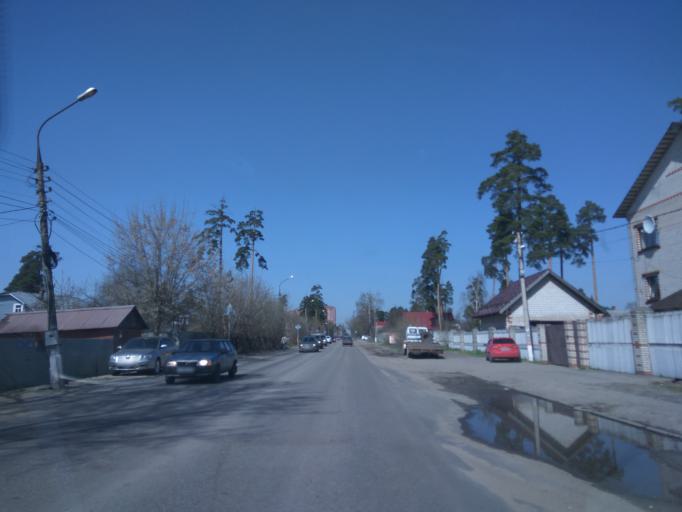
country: RU
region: Moskovskaya
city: Ramenskoye
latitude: 55.5604
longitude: 38.2136
